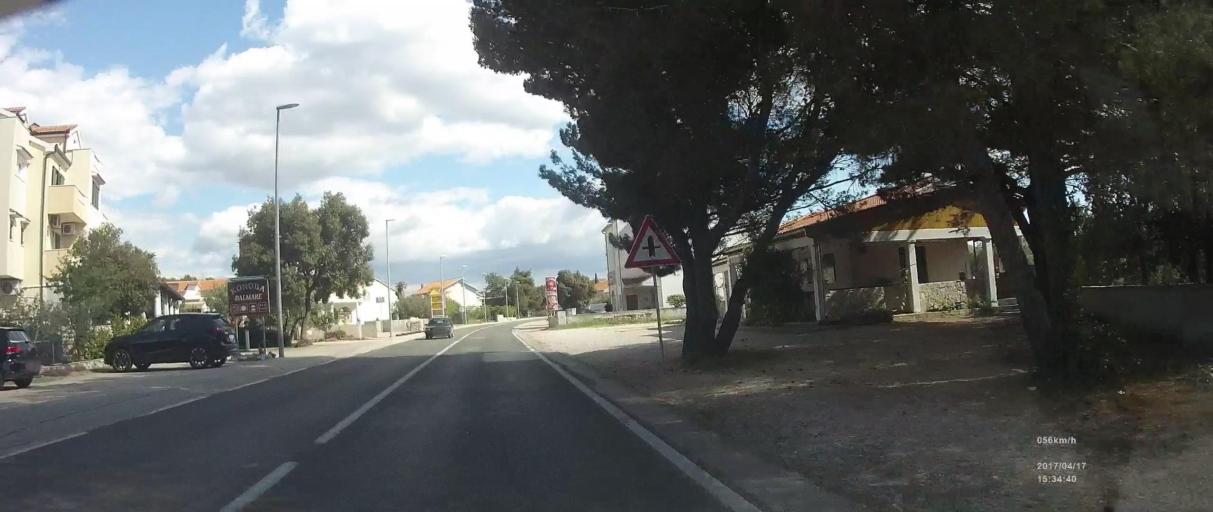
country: HR
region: Sibensko-Kniniska
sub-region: Grad Sibenik
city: Brodarica
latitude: 43.6788
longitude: 15.9202
